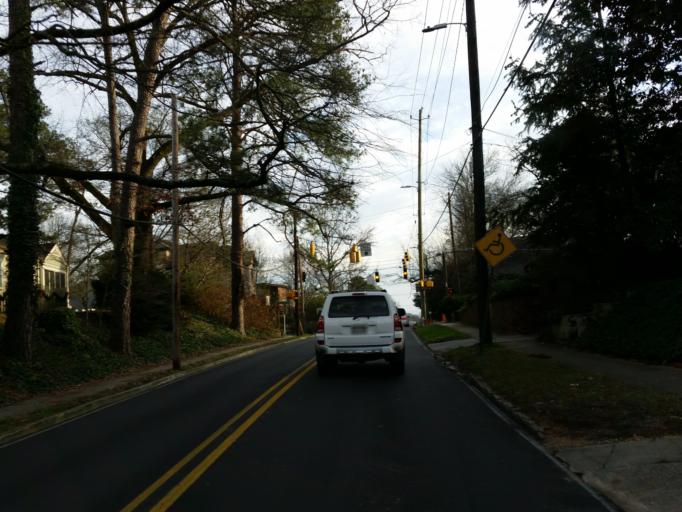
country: US
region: Georgia
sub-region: DeKalb County
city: Druid Hills
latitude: 33.8024
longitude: -84.3726
